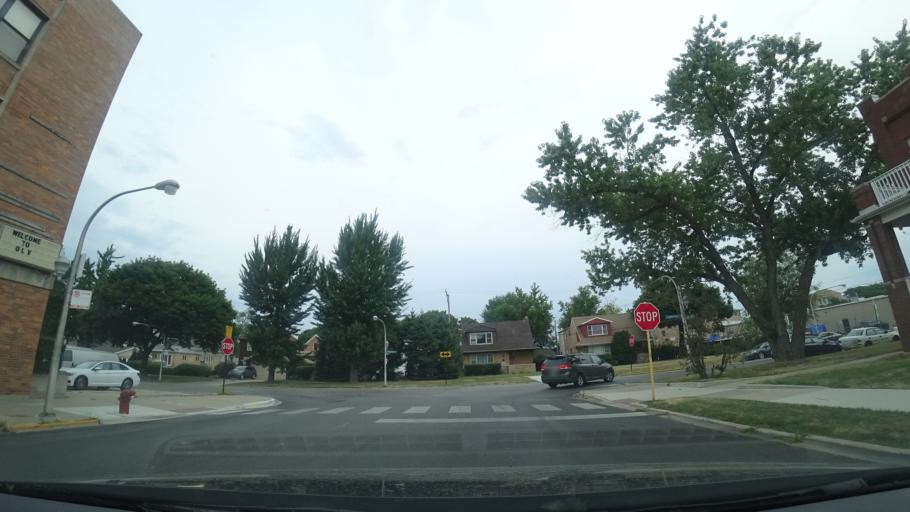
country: US
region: Illinois
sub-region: Cook County
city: Harwood Heights
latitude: 41.9622
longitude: -87.7575
